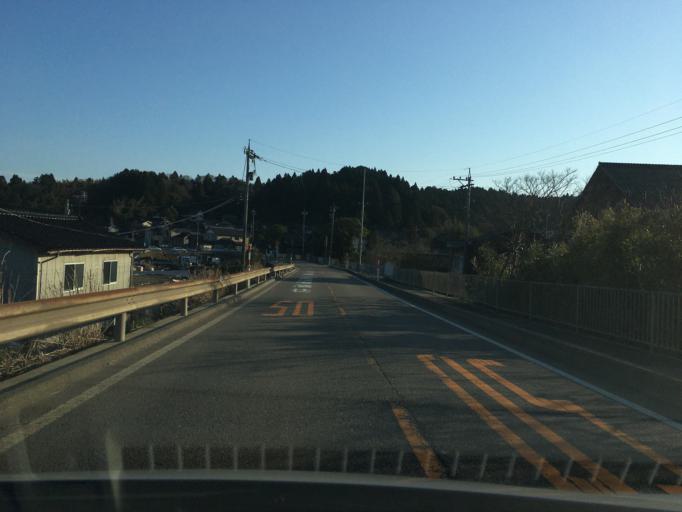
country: JP
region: Ishikawa
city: Nanao
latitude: 36.9787
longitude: 137.0501
